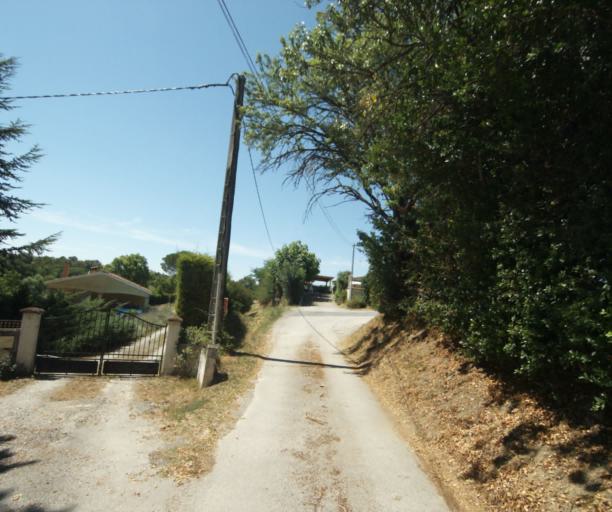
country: FR
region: Midi-Pyrenees
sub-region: Departement de la Haute-Garonne
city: Saint-Felix-Lauragais
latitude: 43.4801
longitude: 1.9208
